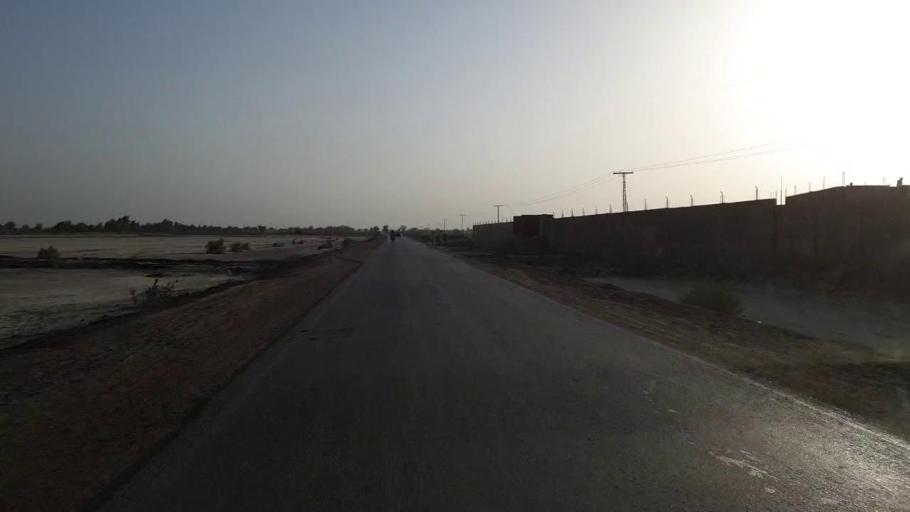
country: PK
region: Sindh
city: Jam Sahib
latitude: 26.2895
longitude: 68.6067
